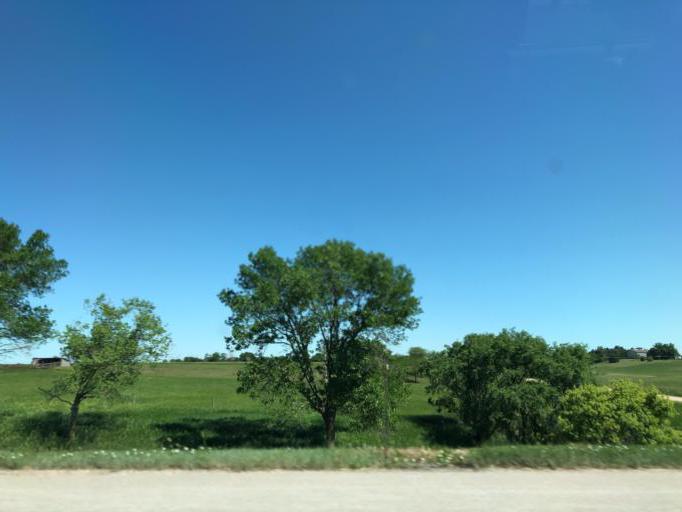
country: US
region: Nebraska
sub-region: York County
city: York
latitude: 40.8213
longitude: -97.4066
